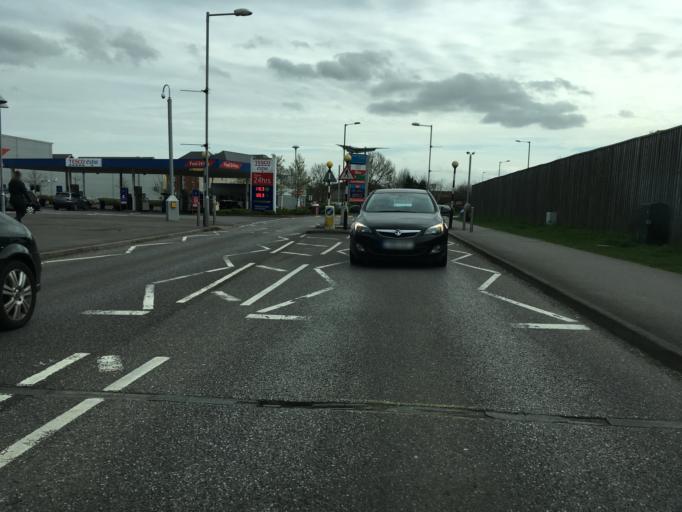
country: GB
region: England
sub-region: South Gloucestershire
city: Stoke Gifford
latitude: 51.5352
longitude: -2.5500
